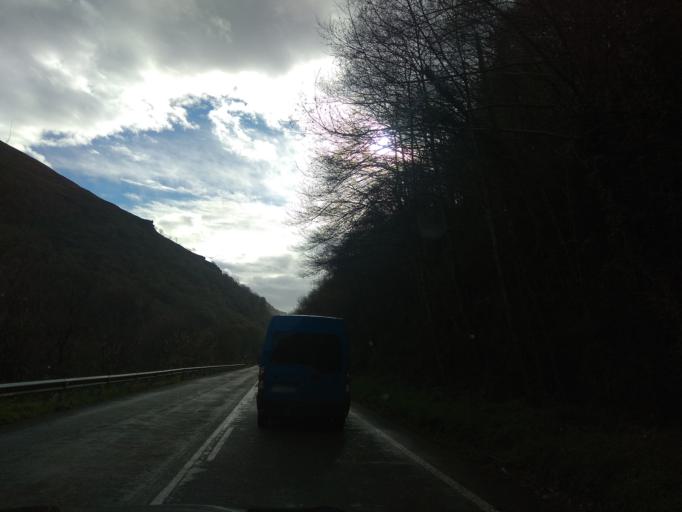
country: ES
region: Cantabria
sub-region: Provincia de Cantabria
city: San Pedro del Romeral
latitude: 43.1387
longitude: -3.9008
